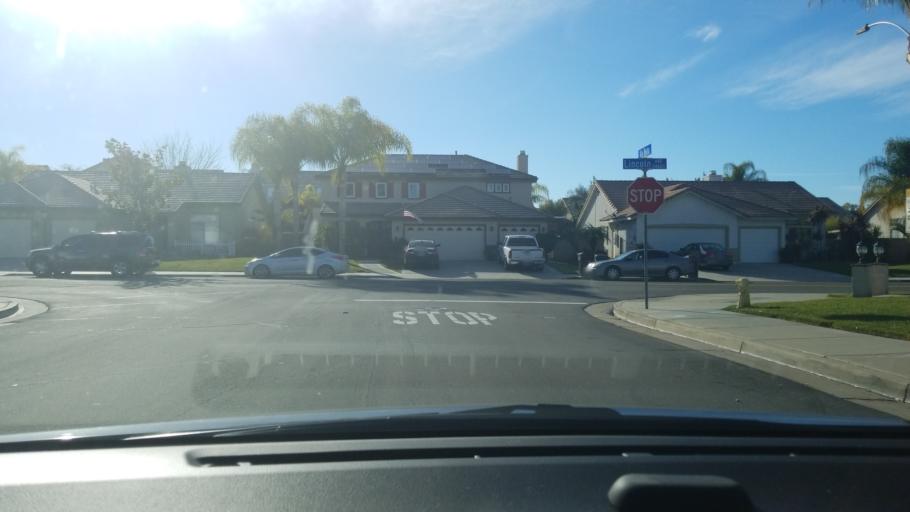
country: US
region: California
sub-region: Riverside County
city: Murrieta
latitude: 33.5708
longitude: -117.1970
